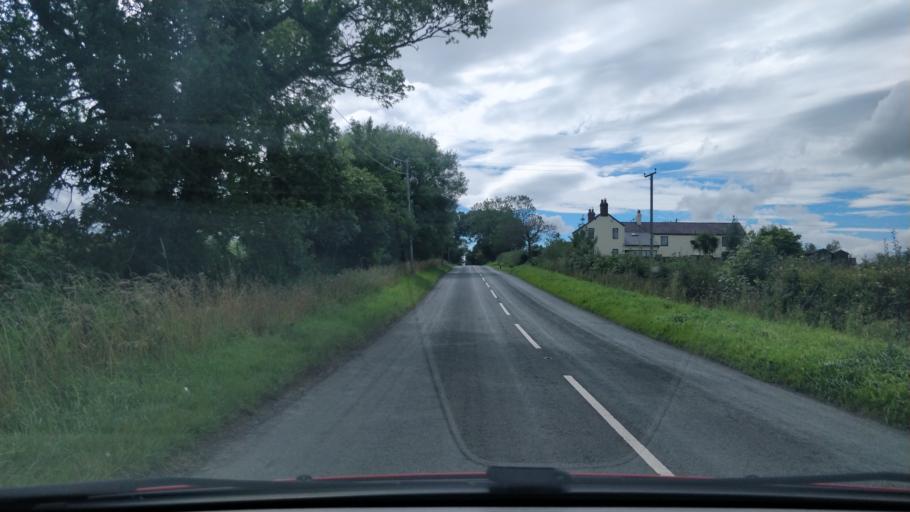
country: GB
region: Wales
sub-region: County of Flintshire
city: Hope
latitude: 53.1300
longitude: -3.0236
